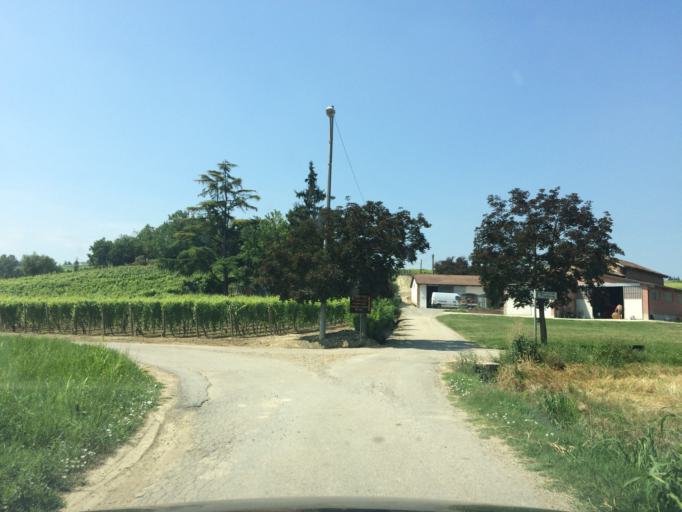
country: IT
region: Piedmont
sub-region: Provincia di Asti
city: Costigliole d'Asti
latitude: 44.7735
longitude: 8.2164
